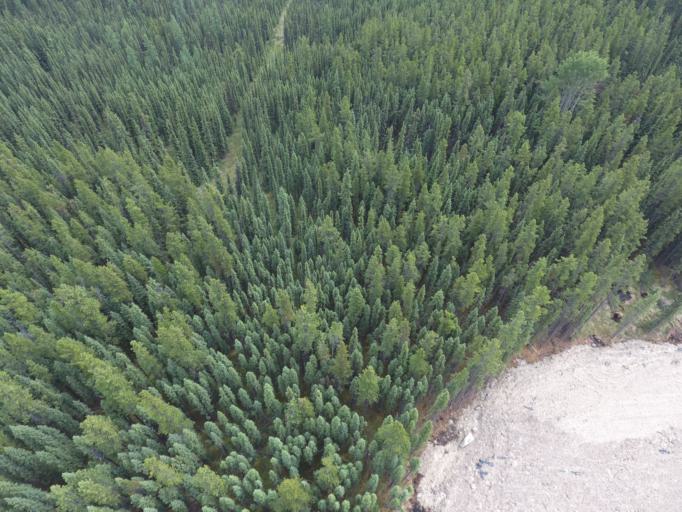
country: CA
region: Alberta
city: Edson
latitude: 52.8431
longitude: -116.0404
